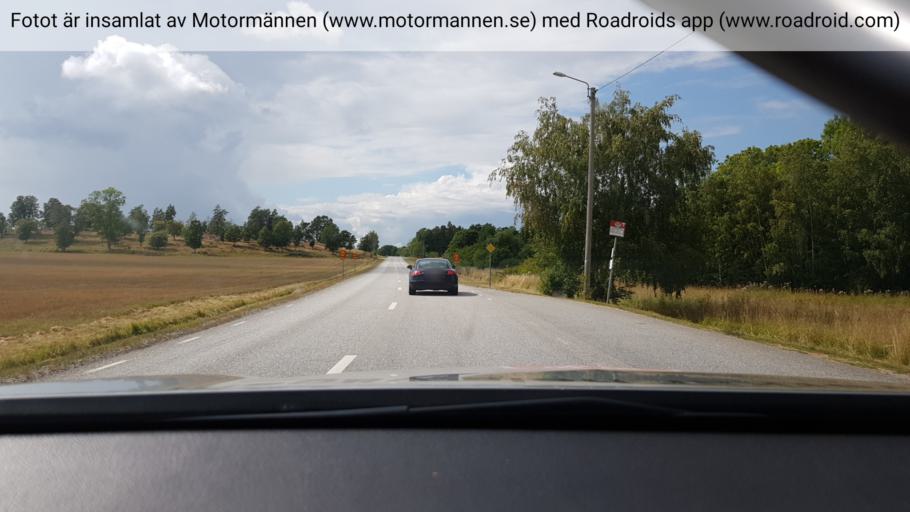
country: SE
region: Stockholm
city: Stenhamra
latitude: 59.3987
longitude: 17.5641
